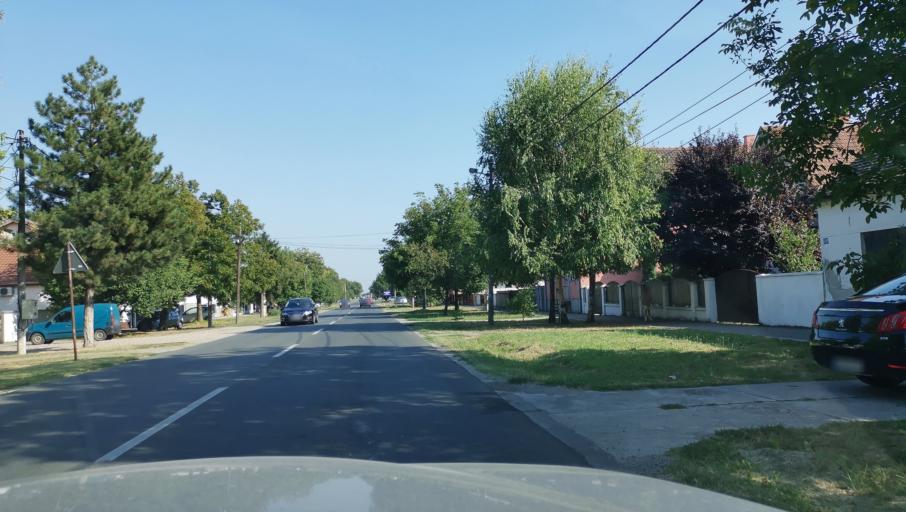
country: RS
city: Dobanovci
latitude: 44.8195
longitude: 20.2298
